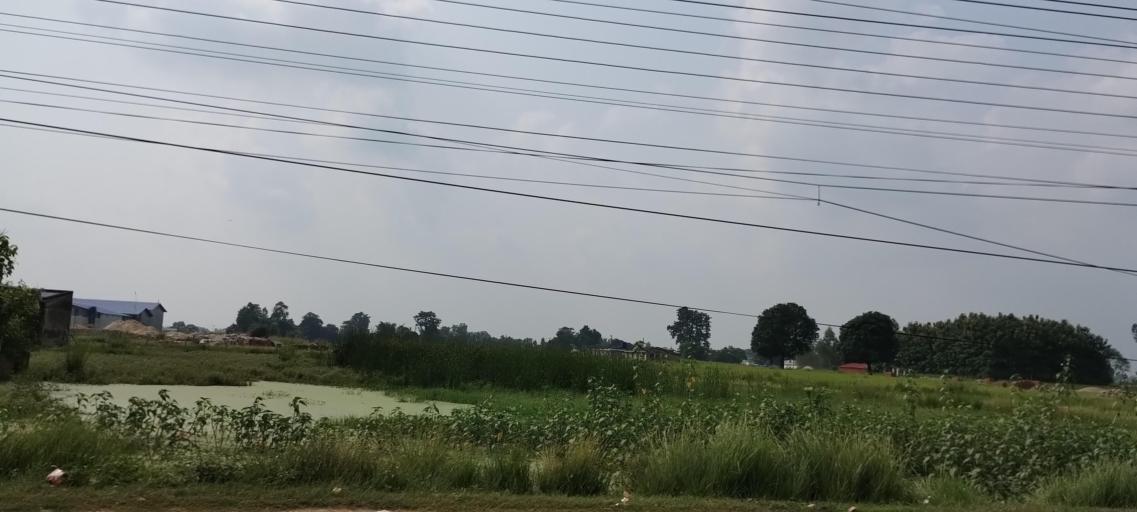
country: NP
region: Mid Western
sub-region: Bheri Zone
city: Nepalgunj
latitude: 28.1646
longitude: 81.6735
